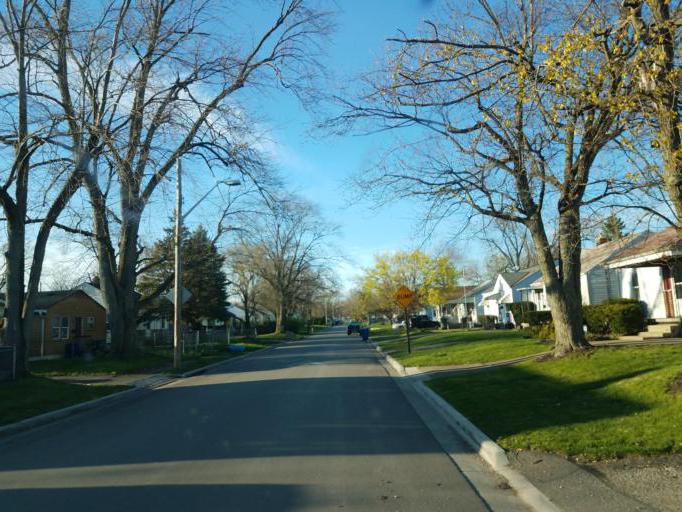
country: US
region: Ohio
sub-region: Franklin County
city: Columbus
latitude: 40.0200
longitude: -82.9895
